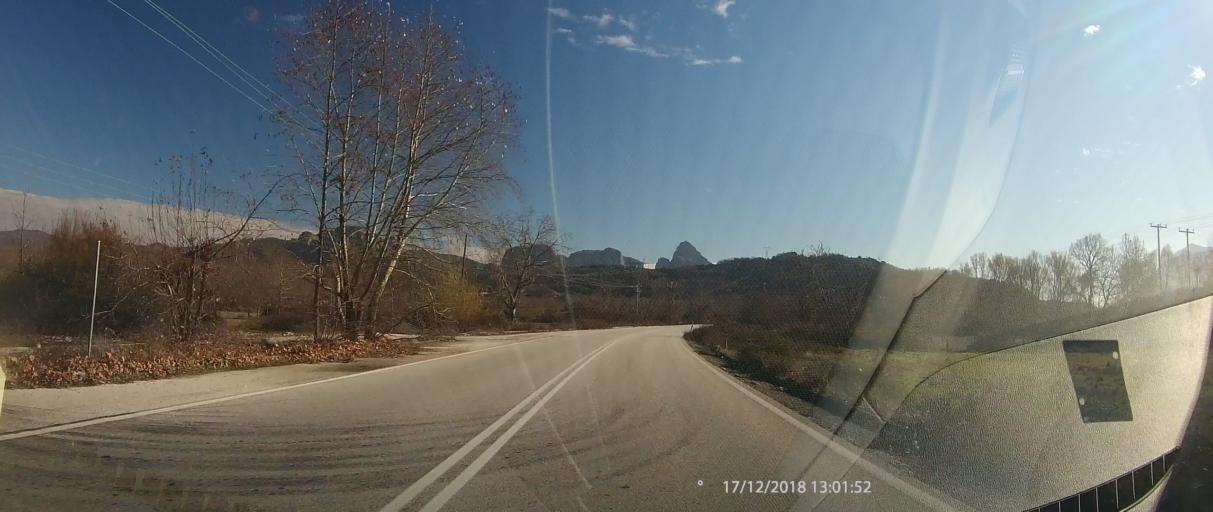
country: GR
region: Thessaly
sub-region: Trikala
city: Kastraki
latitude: 39.7301
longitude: 21.5889
